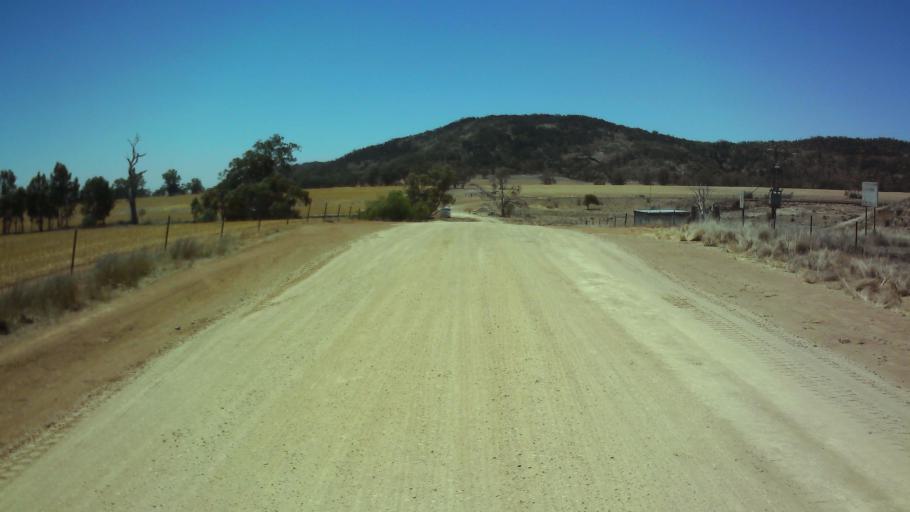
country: AU
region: New South Wales
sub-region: Weddin
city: Grenfell
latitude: -33.8555
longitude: 148.1077
